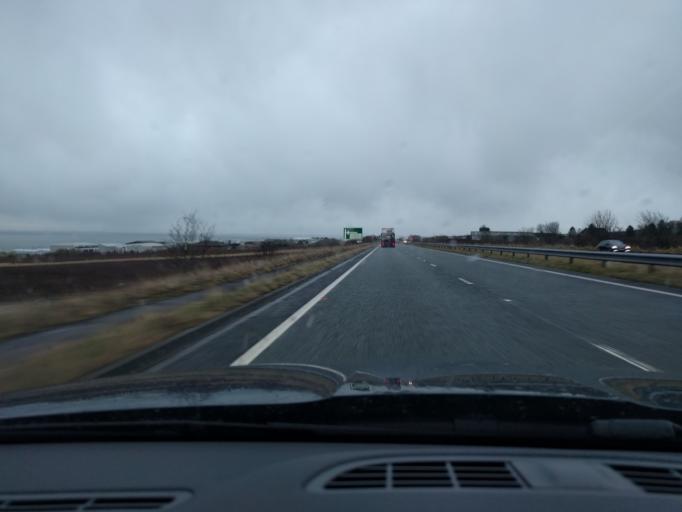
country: GB
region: England
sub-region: Northumberland
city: Berwick-Upon-Tweed
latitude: 55.7927
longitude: -2.0257
